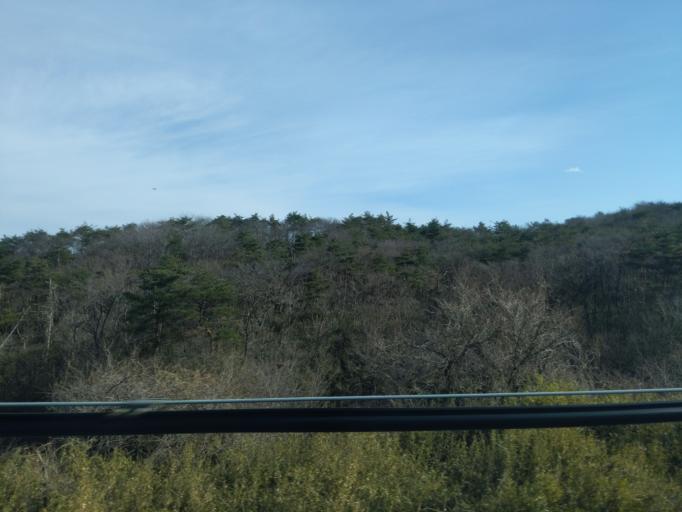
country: JP
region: Miyagi
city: Furukawa
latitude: 38.4695
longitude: 140.9604
